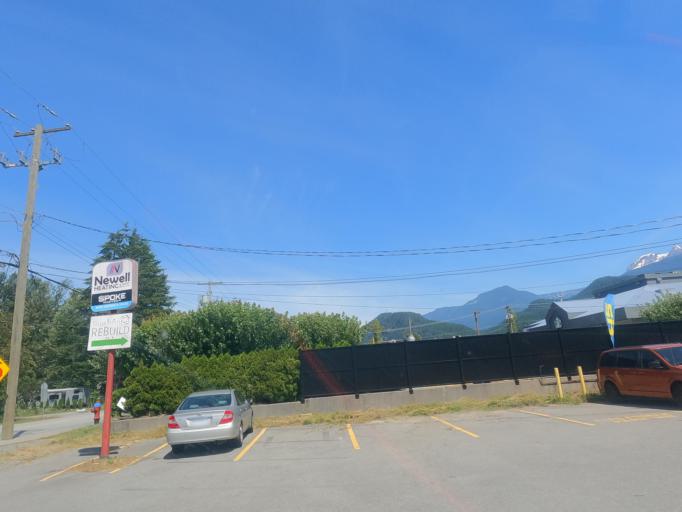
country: CA
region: British Columbia
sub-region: Greater Vancouver Regional District
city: Lions Bay
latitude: 49.7400
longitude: -123.1367
